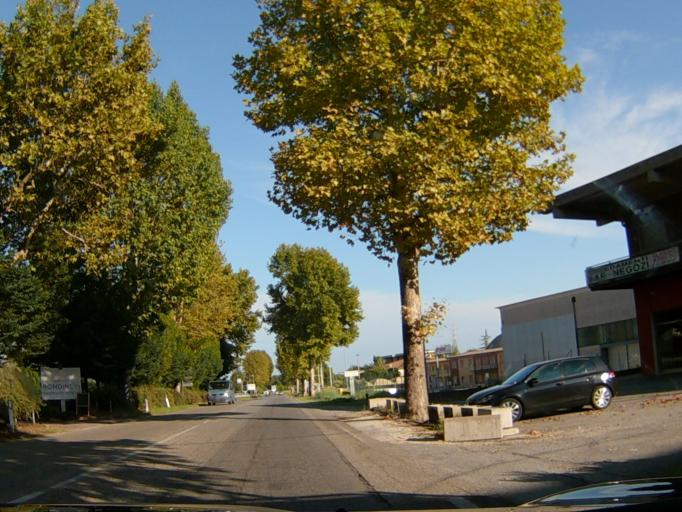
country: IT
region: Lombardy
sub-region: Provincia di Brescia
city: Ponte San Marco
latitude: 45.4775
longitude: 10.3941
